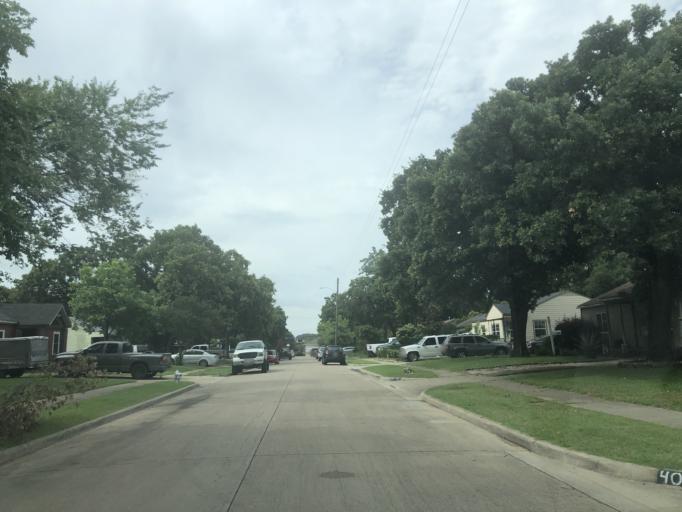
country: US
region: Texas
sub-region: Dallas County
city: Irving
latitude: 32.8102
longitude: -96.9547
